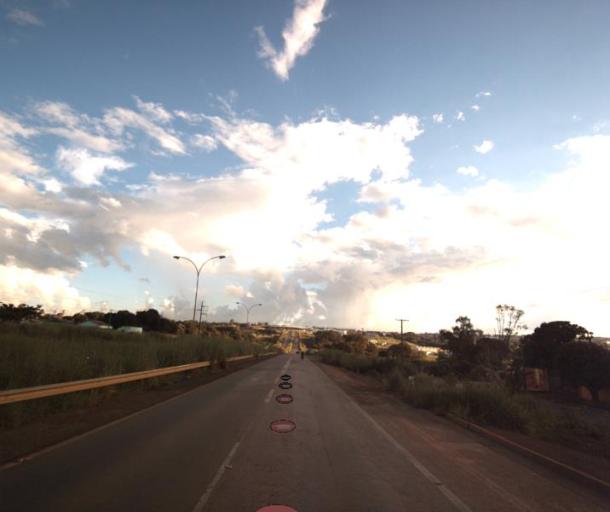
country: BR
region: Goias
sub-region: Anapolis
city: Anapolis
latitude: -16.3436
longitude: -48.9246
